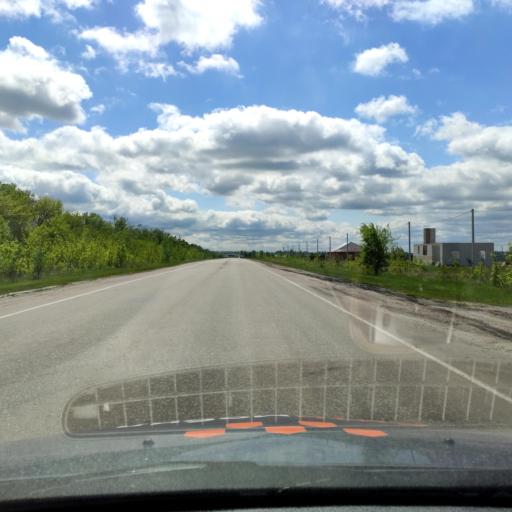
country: RU
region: Voronezj
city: Novaya Usman'
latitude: 51.6163
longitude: 39.3363
